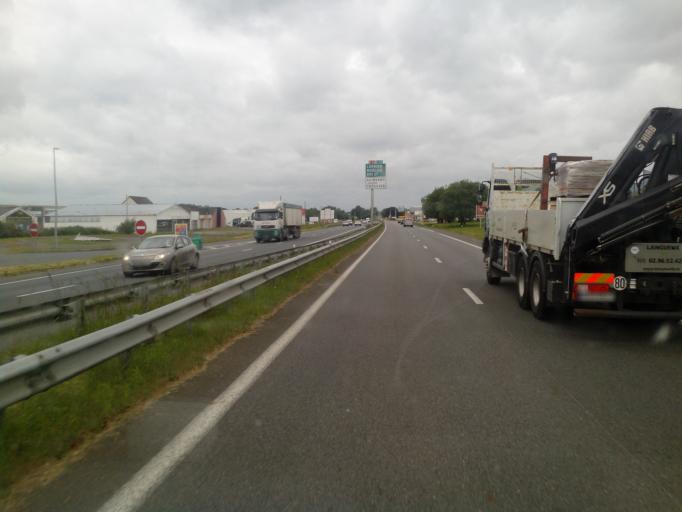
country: FR
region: Brittany
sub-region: Departement des Cotes-d'Armor
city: Saint-Agathon
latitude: 48.5506
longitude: -3.1121
